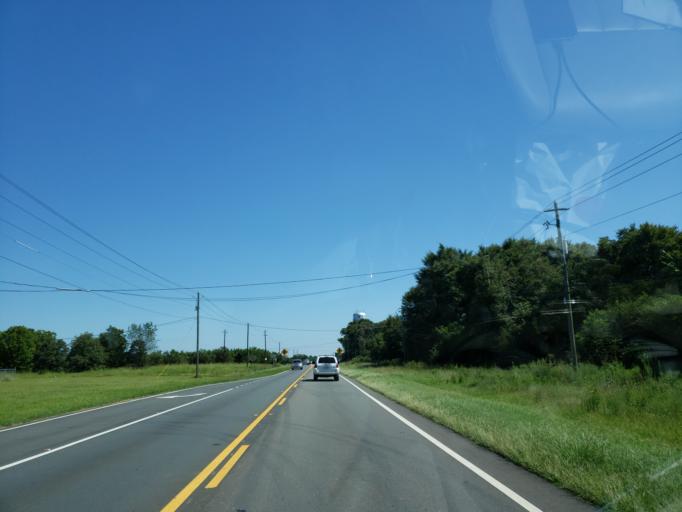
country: US
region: Georgia
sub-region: Peach County
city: Fort Valley
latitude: 32.5305
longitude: -83.8710
